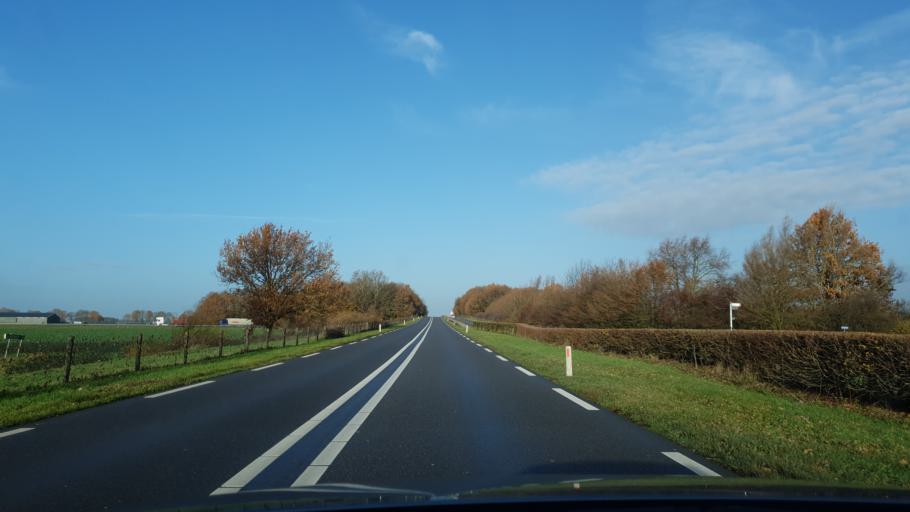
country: NL
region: Gelderland
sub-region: Gemeente Wijchen
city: Bergharen
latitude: 51.8239
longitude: 5.6865
